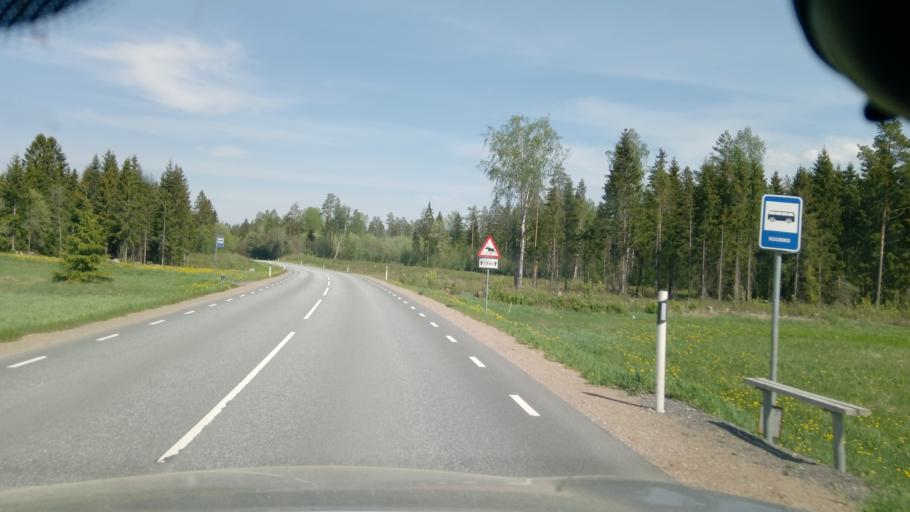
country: EE
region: Laeaene-Virumaa
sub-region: Tapa vald
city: Tapa
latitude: 59.3846
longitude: 26.0160
